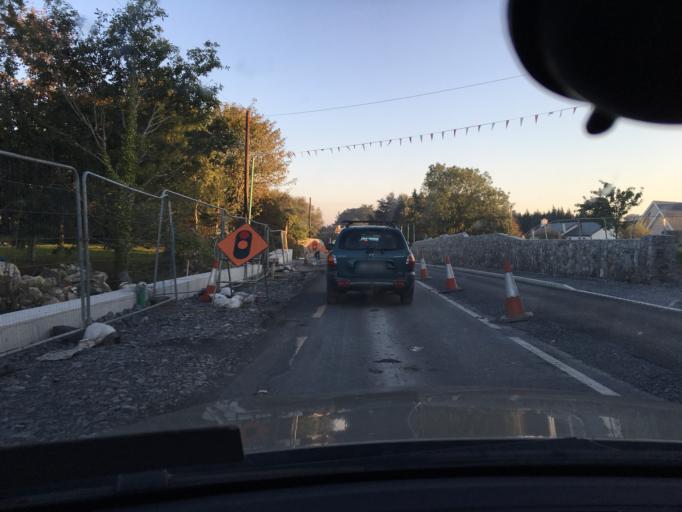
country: IE
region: Connaught
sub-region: County Galway
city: Moycullen
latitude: 53.3278
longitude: -9.1684
